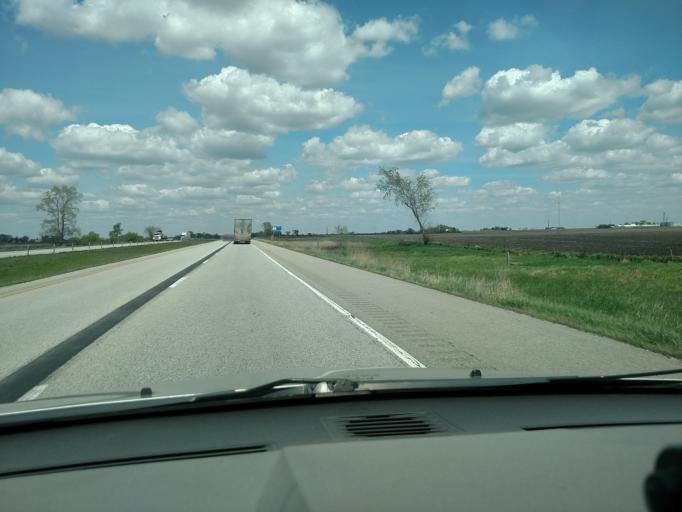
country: US
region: Iowa
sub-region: Polk County
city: Ankeny
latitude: 41.7796
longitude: -93.5706
